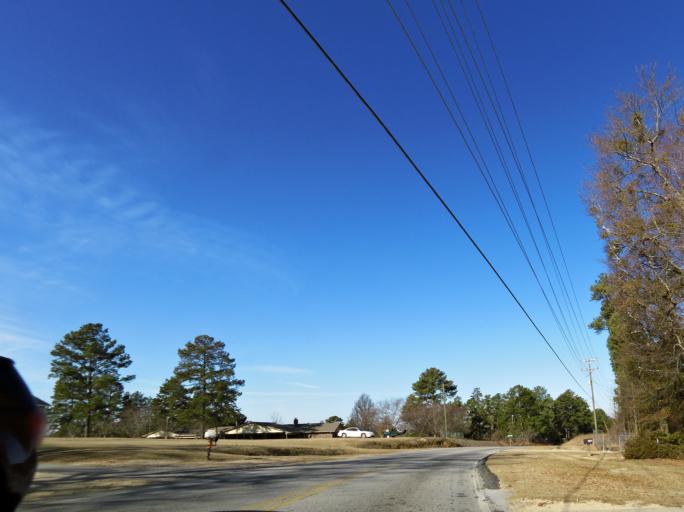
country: US
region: Georgia
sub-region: Bibb County
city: West Point
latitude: 32.7475
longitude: -83.7374
